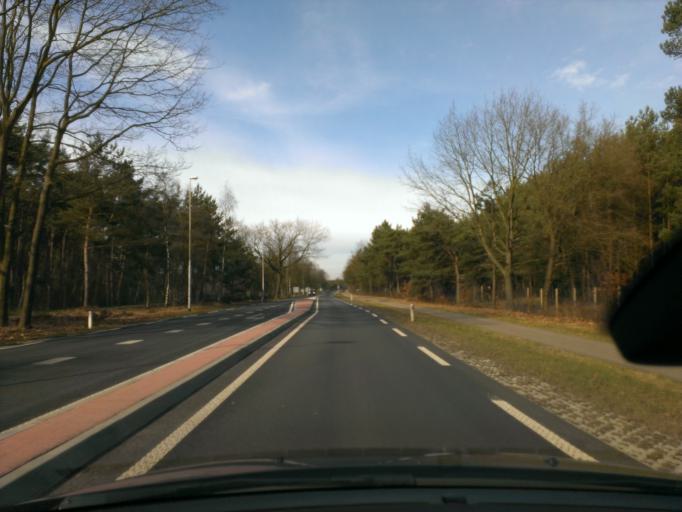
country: NL
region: Gelderland
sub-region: Gemeente Oldebroek
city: Oldebroek
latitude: 52.3959
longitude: 5.9015
